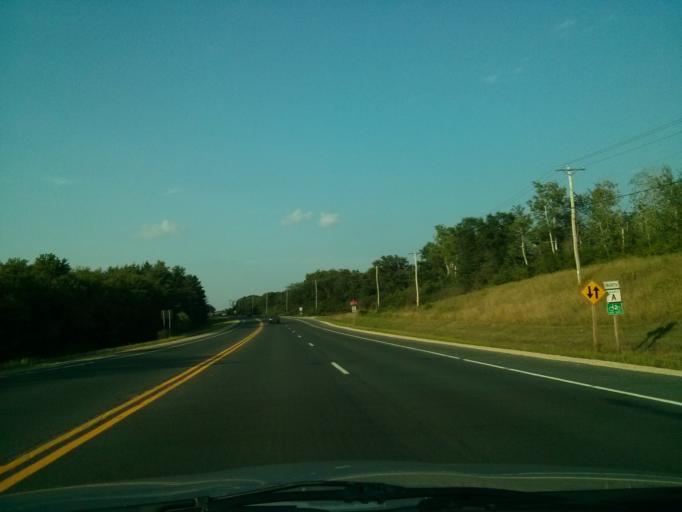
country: US
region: Wisconsin
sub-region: Saint Croix County
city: North Hudson
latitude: 44.9931
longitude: -92.6793
